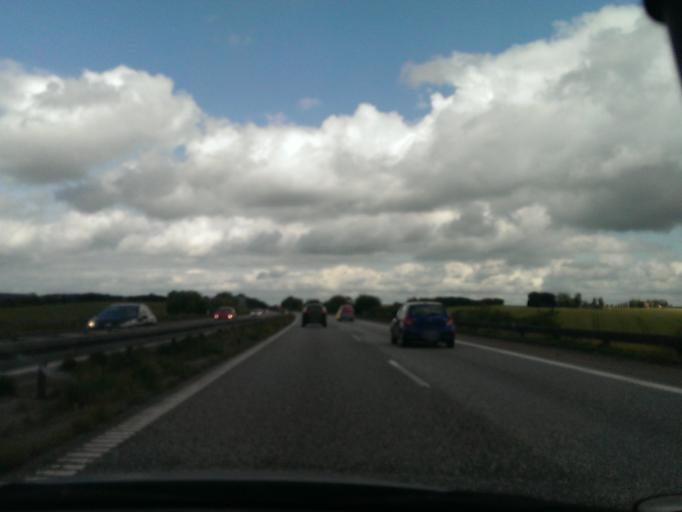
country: DK
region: North Denmark
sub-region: Mariagerfjord Kommune
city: Hobro
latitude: 56.5993
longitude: 9.7580
